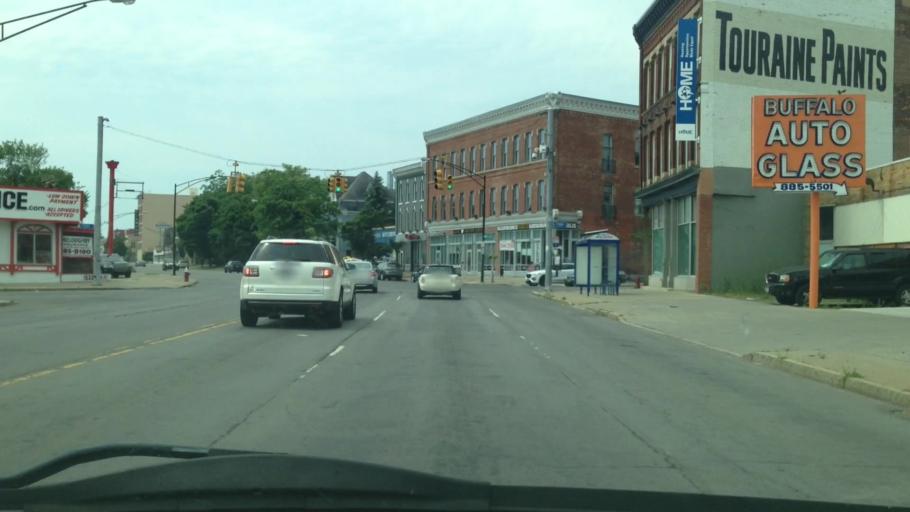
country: US
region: New York
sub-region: Erie County
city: Buffalo
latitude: 42.9158
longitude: -78.8641
